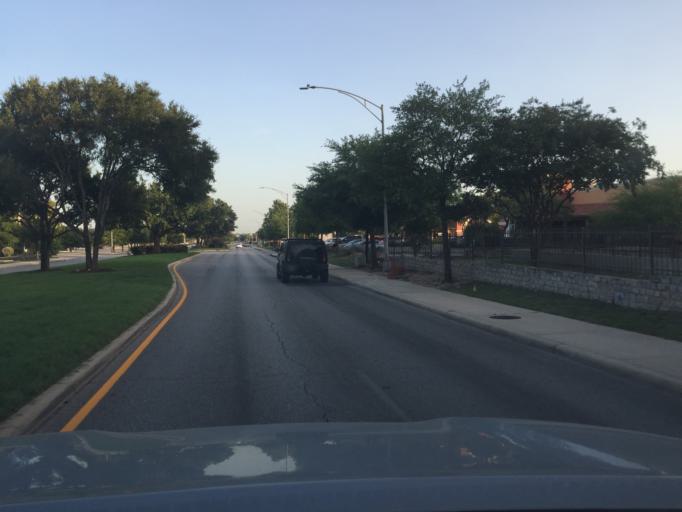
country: US
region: Texas
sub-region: Bexar County
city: Hollywood Park
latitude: 29.6298
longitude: -98.4954
